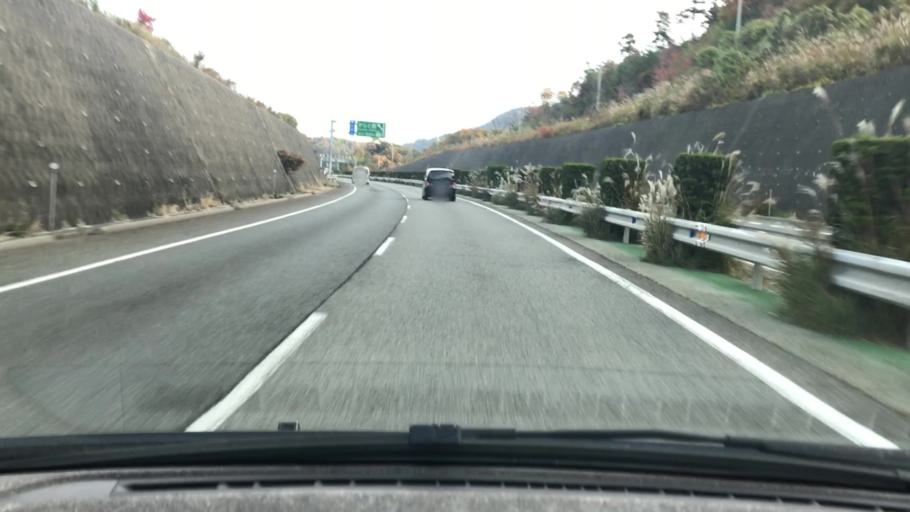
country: JP
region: Hyogo
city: Kobe
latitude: 34.7643
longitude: 135.1951
